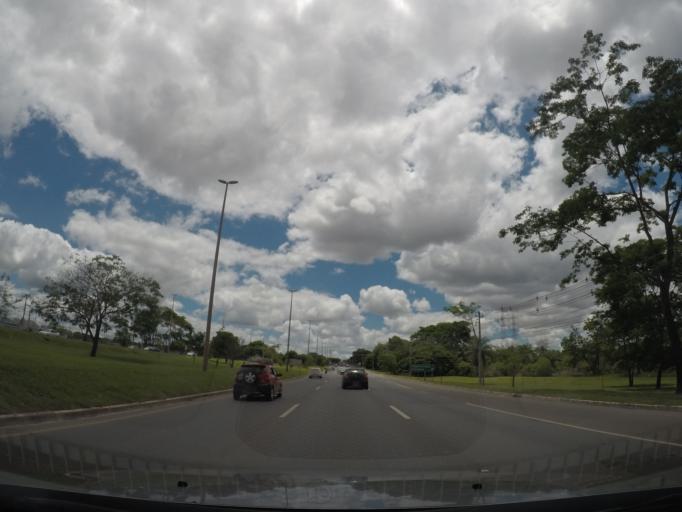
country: BR
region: Federal District
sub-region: Brasilia
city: Brasilia
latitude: -15.7376
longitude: -47.9156
